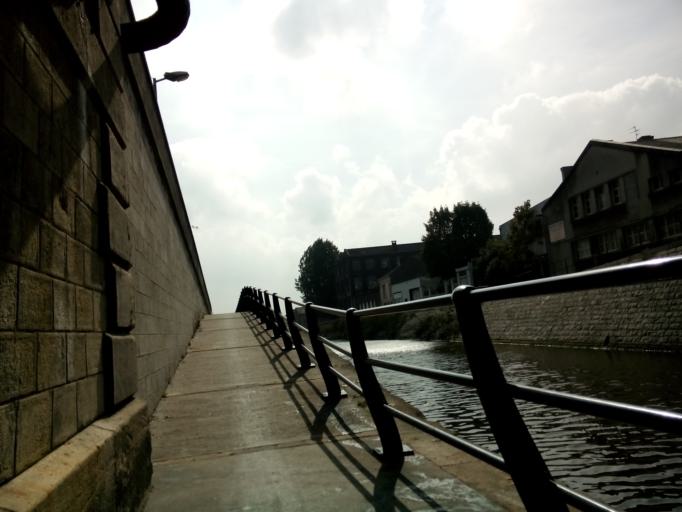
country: FR
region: Nord-Pas-de-Calais
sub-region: Departement du Pas-de-Calais
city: Calais
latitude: 50.9453
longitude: 1.8658
